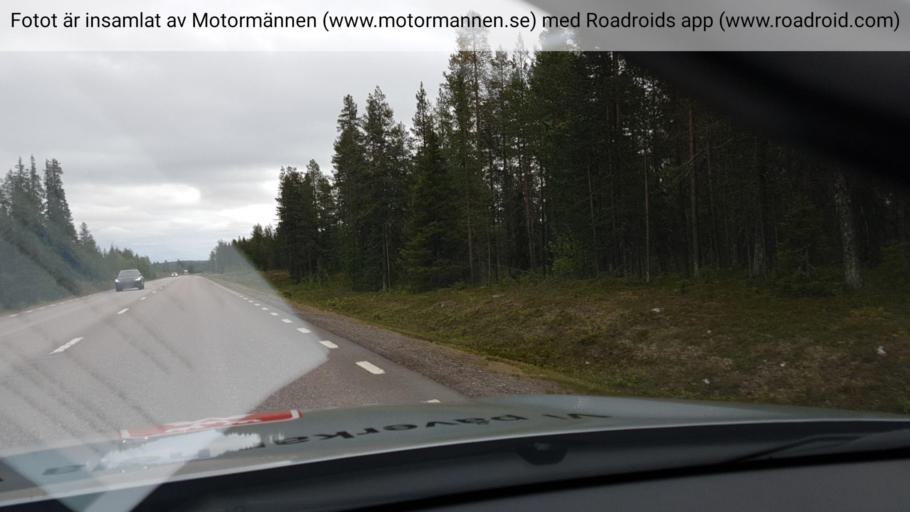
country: SE
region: Norrbotten
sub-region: Gallivare Kommun
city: Gaellivare
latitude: 67.0782
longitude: 21.0723
